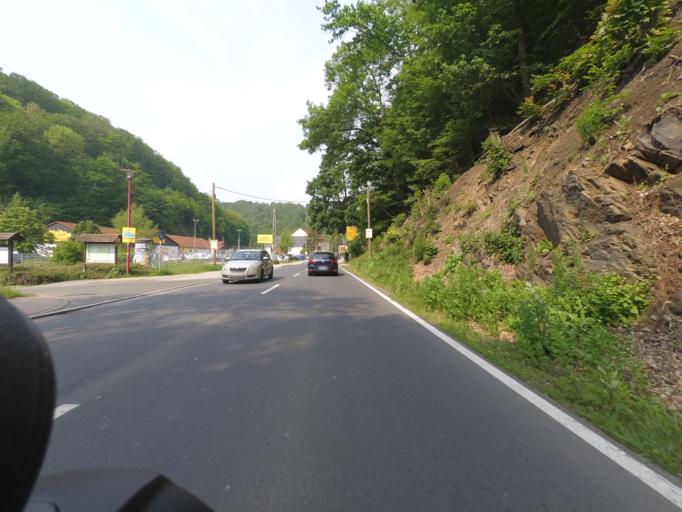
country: DE
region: Saxony
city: Tharandt
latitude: 50.9833
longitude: 13.5884
